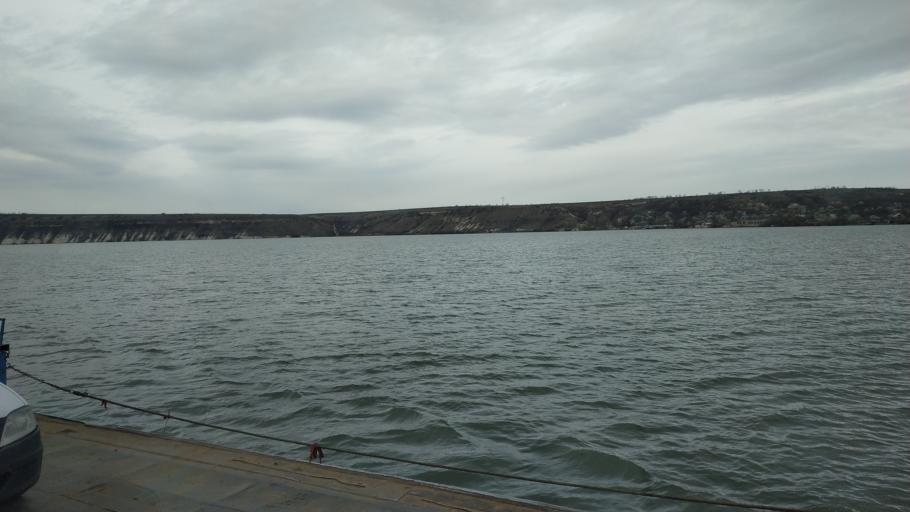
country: MD
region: Telenesti
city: Cocieri
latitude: 47.3508
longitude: 29.1007
